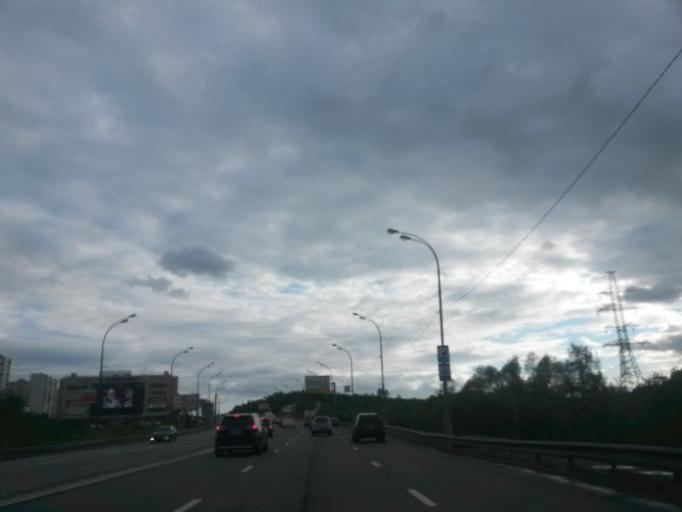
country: RU
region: Moscow
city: Chertanovo Yuzhnoye
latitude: 55.5768
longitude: 37.5670
